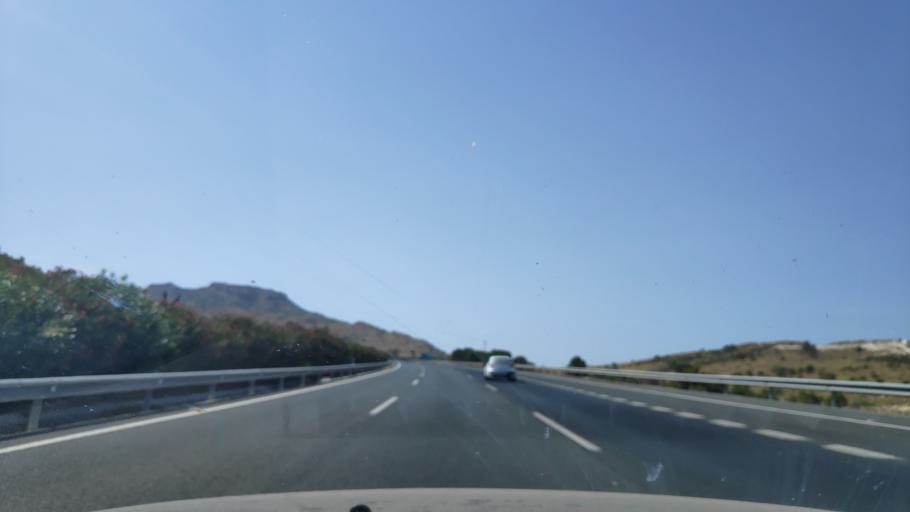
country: ES
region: Murcia
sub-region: Murcia
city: Ulea
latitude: 38.1634
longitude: -1.3022
